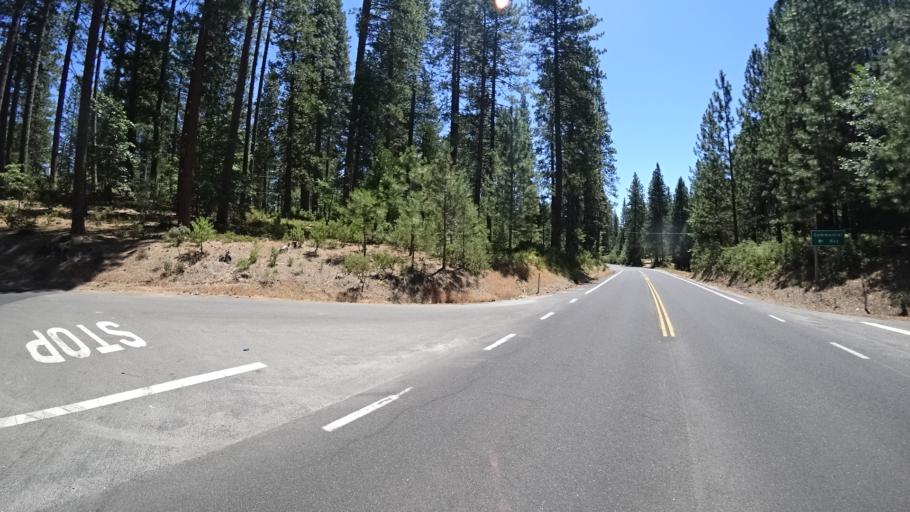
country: US
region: California
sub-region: Calaveras County
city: Forest Meadows
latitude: 38.1969
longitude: -120.3661
